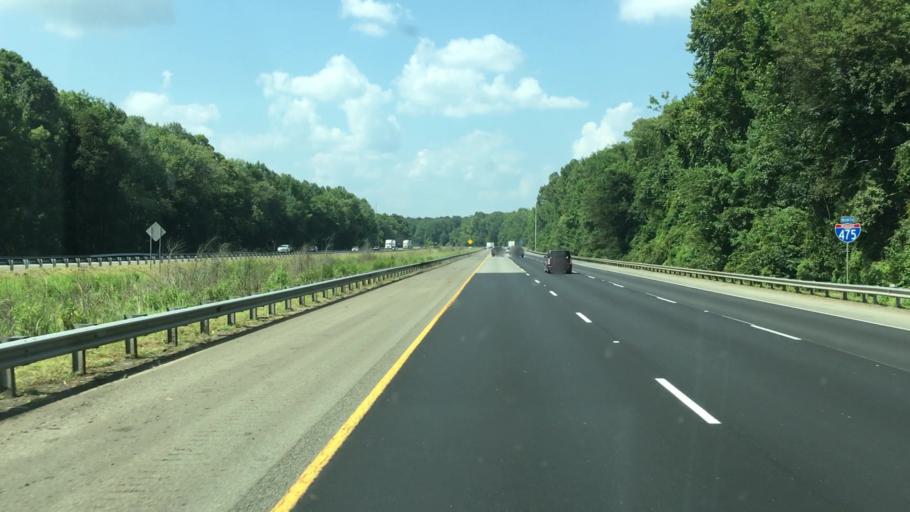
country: US
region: Georgia
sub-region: Bibb County
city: West Point
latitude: 32.7664
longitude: -83.7103
